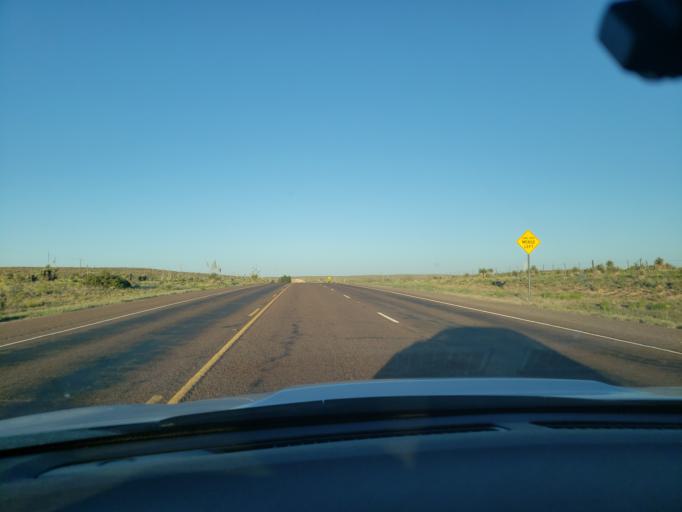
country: US
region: Texas
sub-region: El Paso County
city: Homestead Meadows South
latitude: 31.8271
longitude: -105.8861
